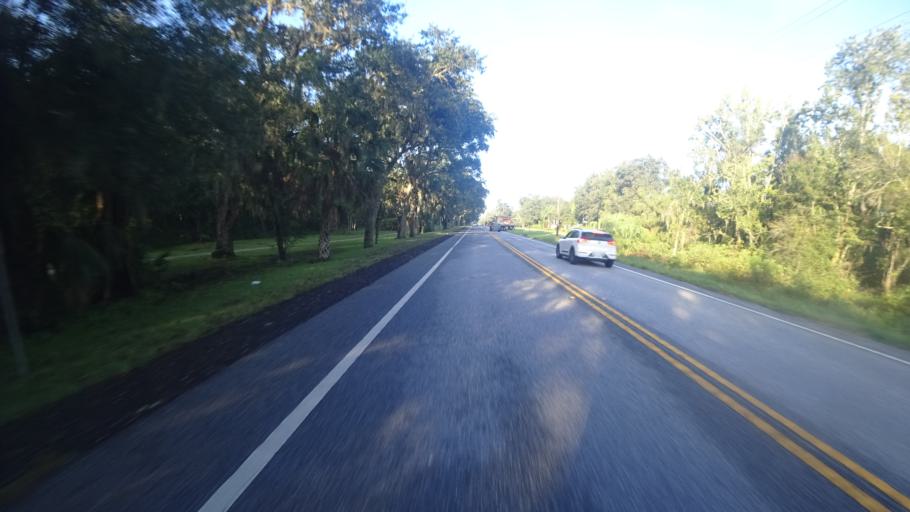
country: US
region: Florida
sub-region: Manatee County
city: Ellenton
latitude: 27.5485
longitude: -82.4403
